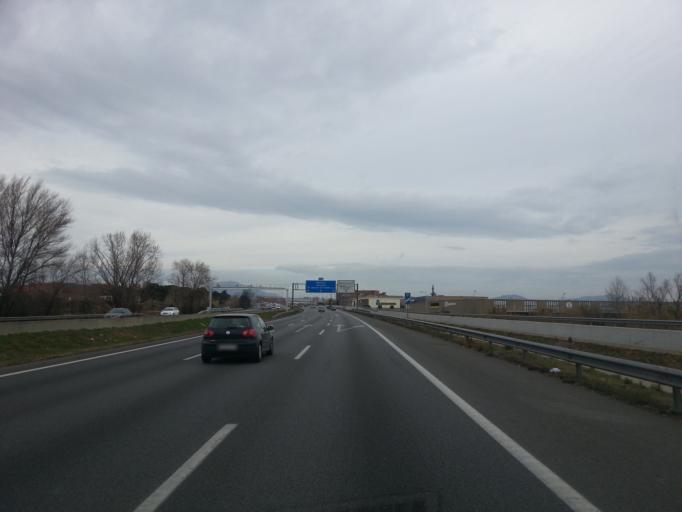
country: ES
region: Catalonia
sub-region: Provincia de Barcelona
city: Sant Quirze del Valles
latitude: 41.5233
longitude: 2.0968
